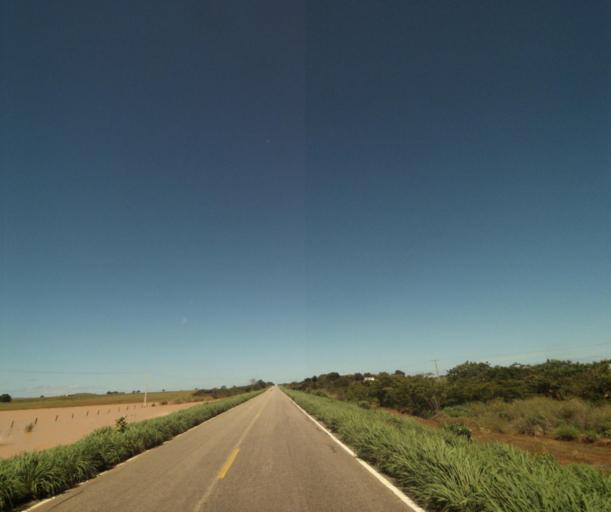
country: BR
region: Bahia
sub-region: Palmas De Monte Alto
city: Palmas de Monte Alto
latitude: -14.2676
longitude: -43.3837
